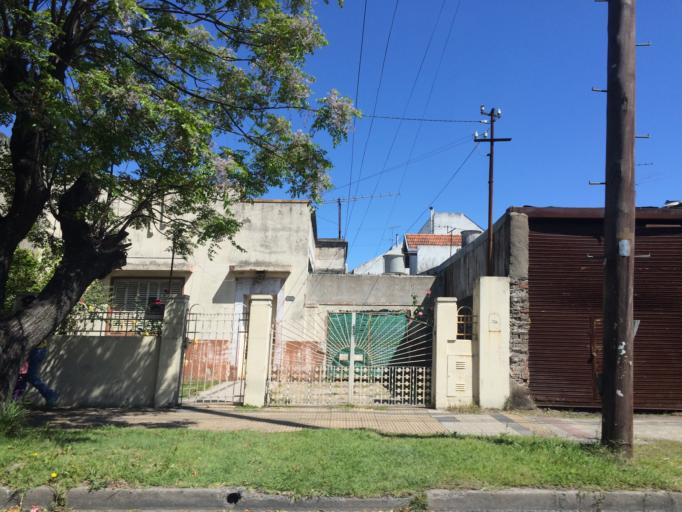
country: AR
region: Buenos Aires
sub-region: Partido de Lanus
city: Lanus
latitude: -34.7232
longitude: -58.3995
